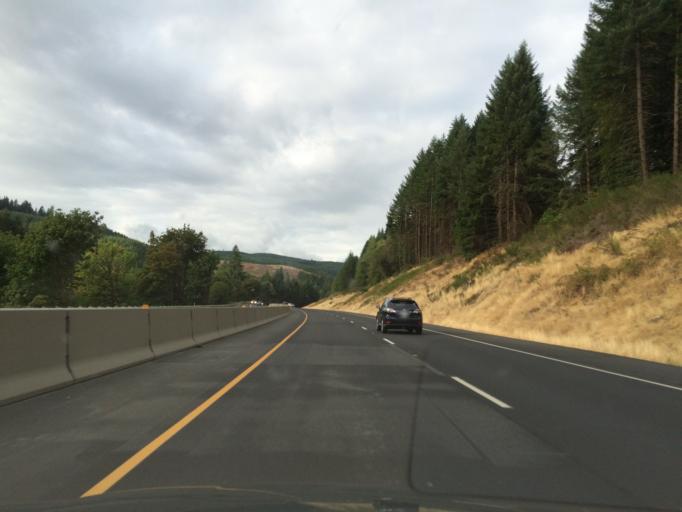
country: US
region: Oregon
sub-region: Lane County
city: Cottage Grove
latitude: 43.7419
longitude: -123.1830
